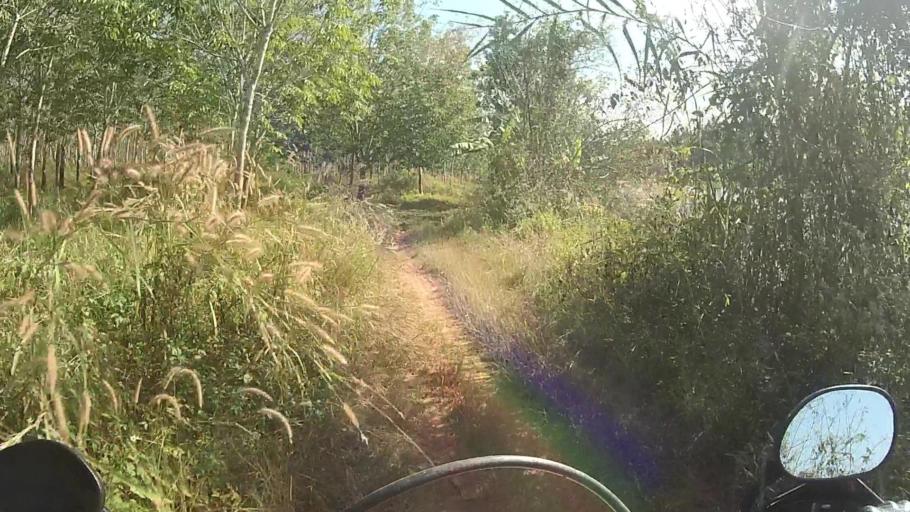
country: TH
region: Chiang Mai
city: Mae On
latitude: 18.9171
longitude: 99.2012
